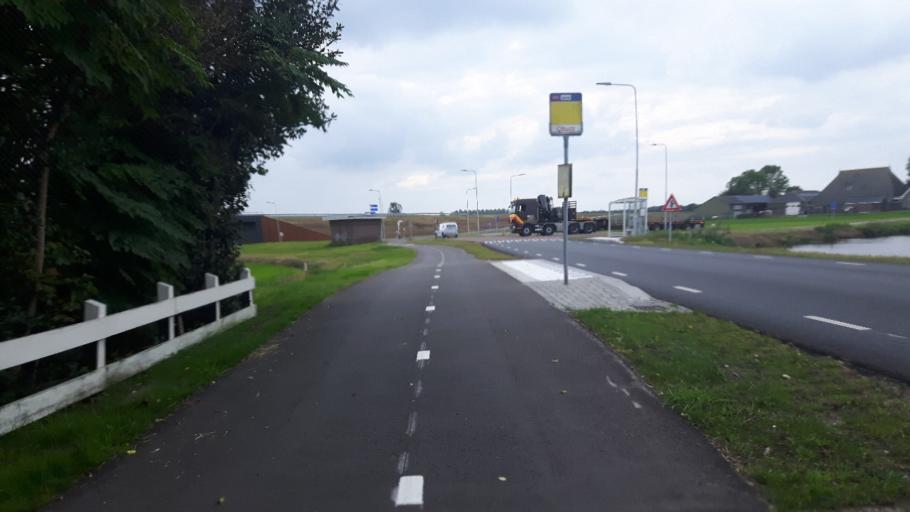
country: NL
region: Friesland
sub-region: Gemeente Heerenveen
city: Jubbega
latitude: 52.9919
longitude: 6.2657
